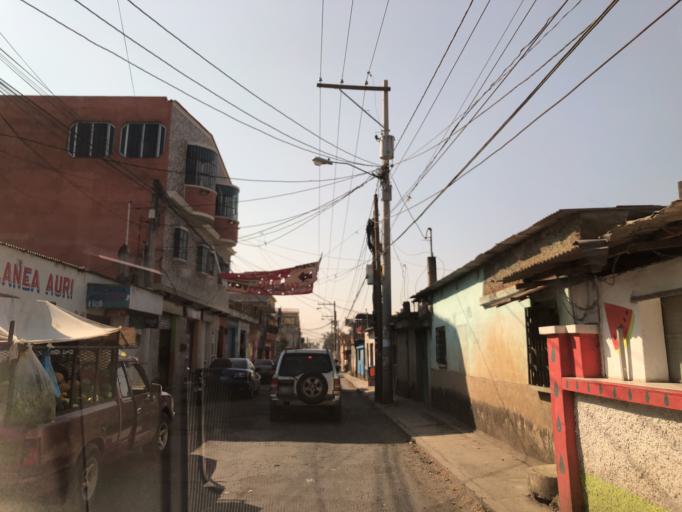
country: GT
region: Guatemala
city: Santa Catarina Pinula
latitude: 14.5421
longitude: -90.5247
